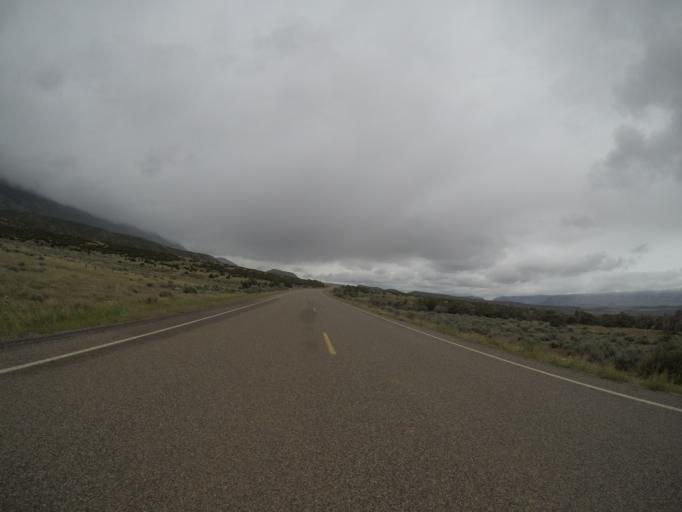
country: US
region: Wyoming
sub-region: Big Horn County
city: Lovell
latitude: 45.0887
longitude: -108.2512
